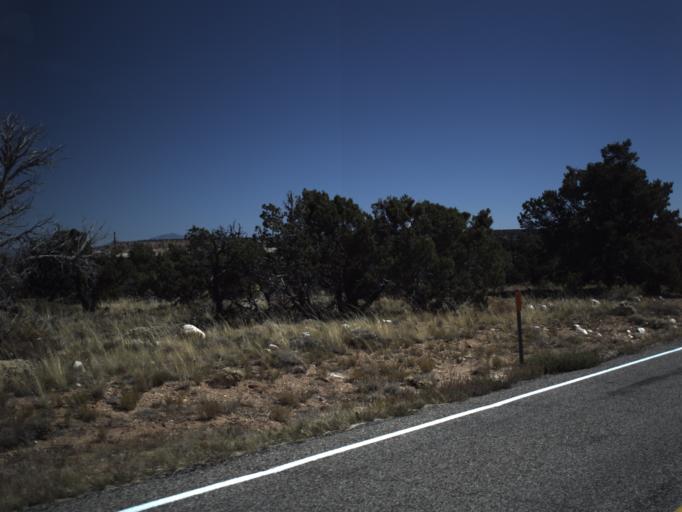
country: US
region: Utah
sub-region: Wayne County
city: Loa
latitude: 37.8751
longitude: -111.4501
